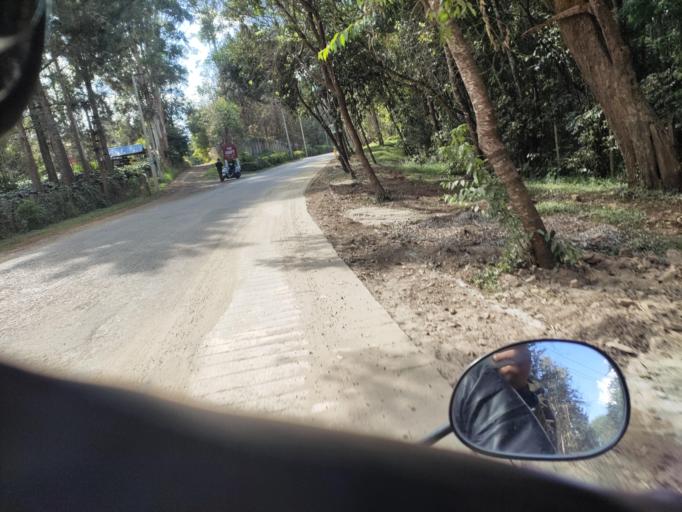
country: MM
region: Mandalay
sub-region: Pyin Oo Lwin District
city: Pyin Oo Lwin
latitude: 21.9909
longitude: 96.4725
